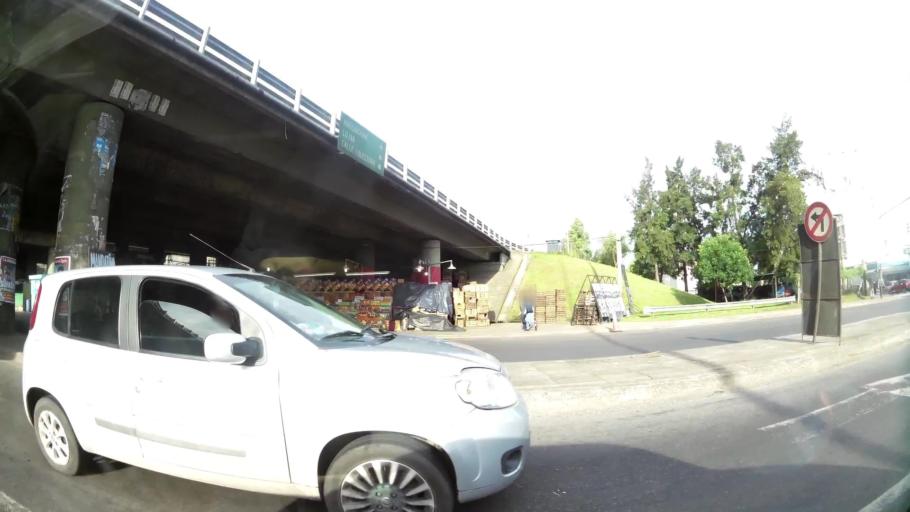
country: AR
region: Buenos Aires
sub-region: Partido de Moron
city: Moron
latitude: -34.6330
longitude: -58.6292
